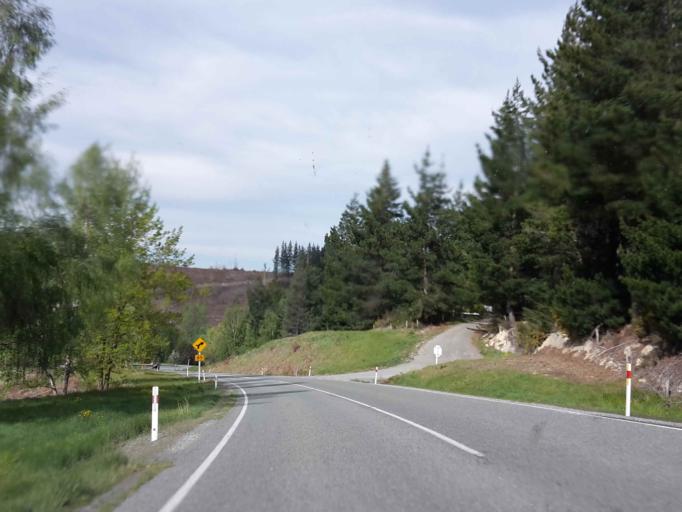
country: NZ
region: Canterbury
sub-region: Timaru District
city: Pleasant Point
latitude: -44.1245
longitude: 171.0782
